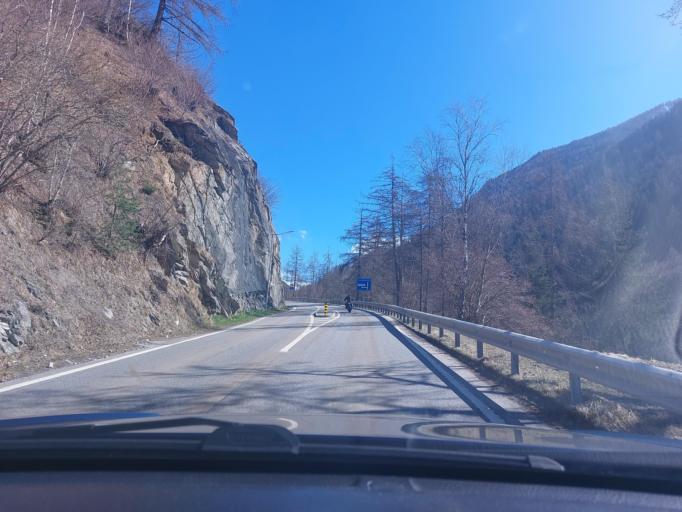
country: CH
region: Valais
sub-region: Herens District
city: Evolene
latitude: 46.1496
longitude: 7.4551
